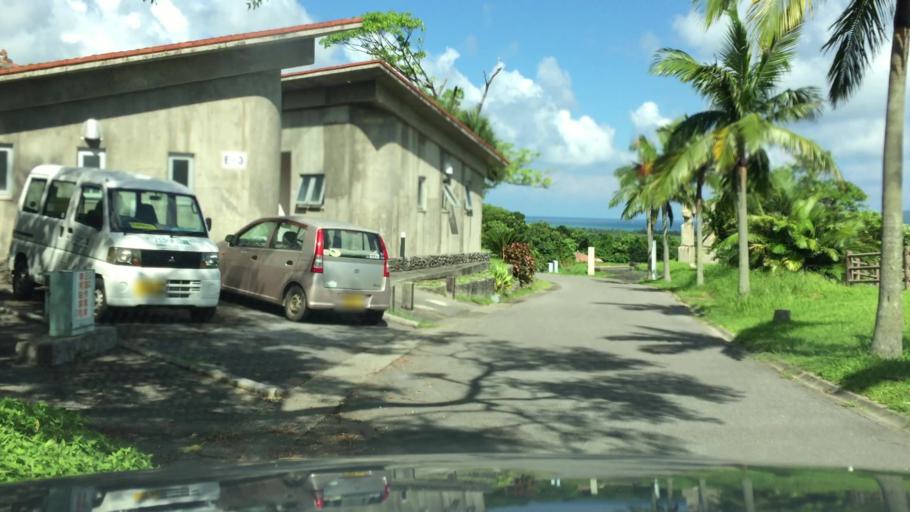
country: JP
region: Okinawa
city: Ishigaki
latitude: 24.3866
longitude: 124.1621
